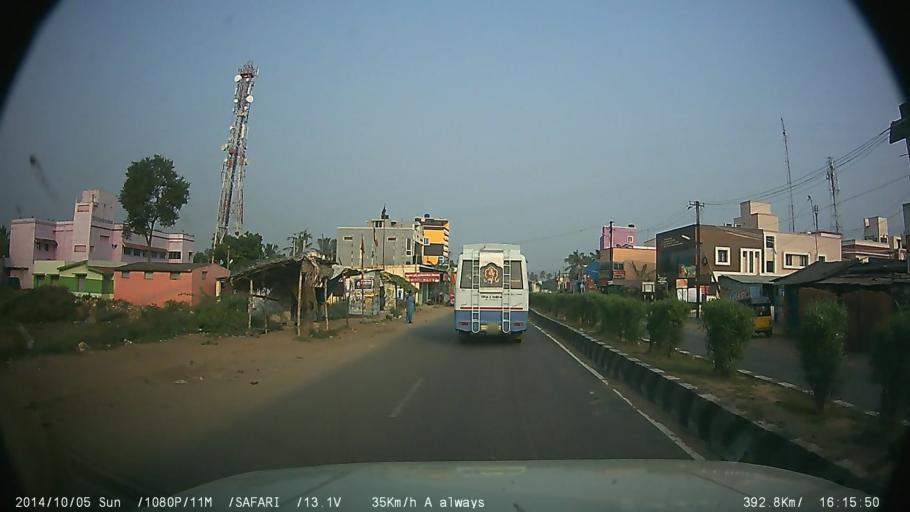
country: IN
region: Tamil Nadu
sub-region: Kancheepuram
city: Vandalur
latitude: 12.8706
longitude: 80.1065
